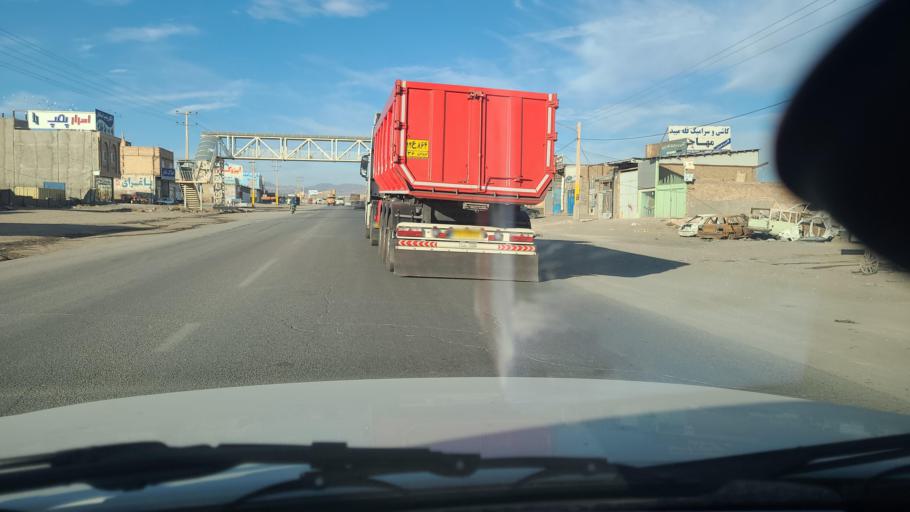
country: IR
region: Razavi Khorasan
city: Sabzevar
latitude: 36.2210
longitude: 57.6515
